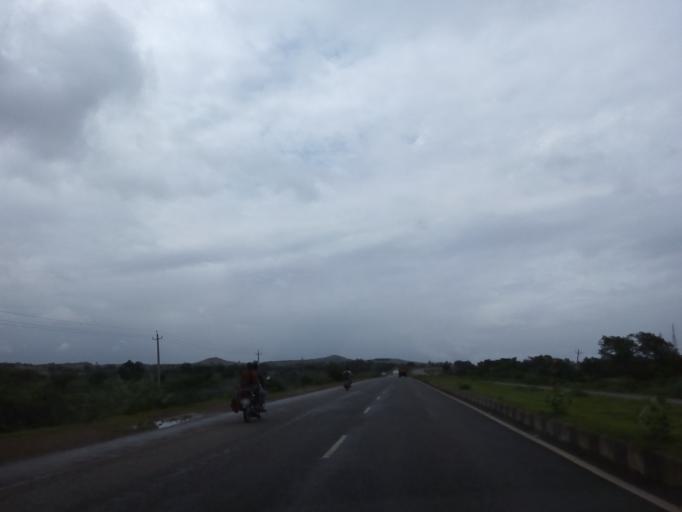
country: IN
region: Karnataka
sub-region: Haveri
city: Byadgi
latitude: 14.7233
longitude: 75.4765
